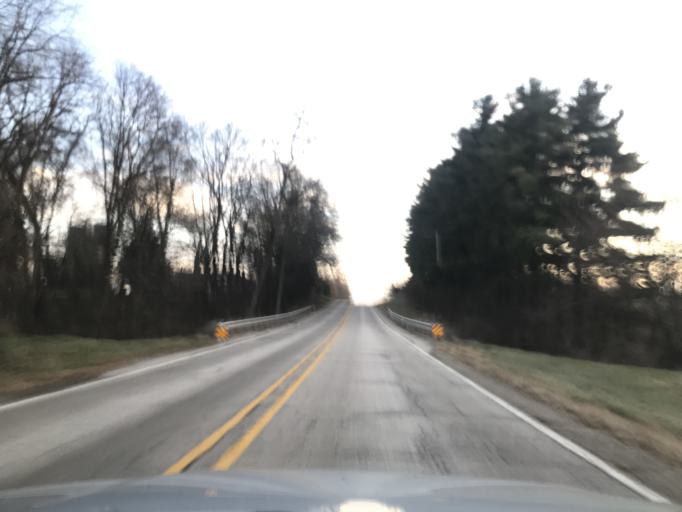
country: US
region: Illinois
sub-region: Henderson County
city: Oquawka
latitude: 40.9372
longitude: -90.8641
